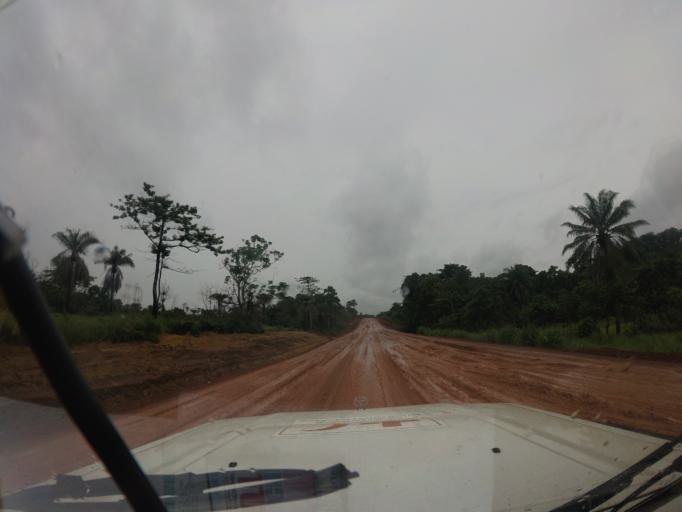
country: SL
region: Eastern Province
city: Tefeya
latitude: 8.5751
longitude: -11.3201
